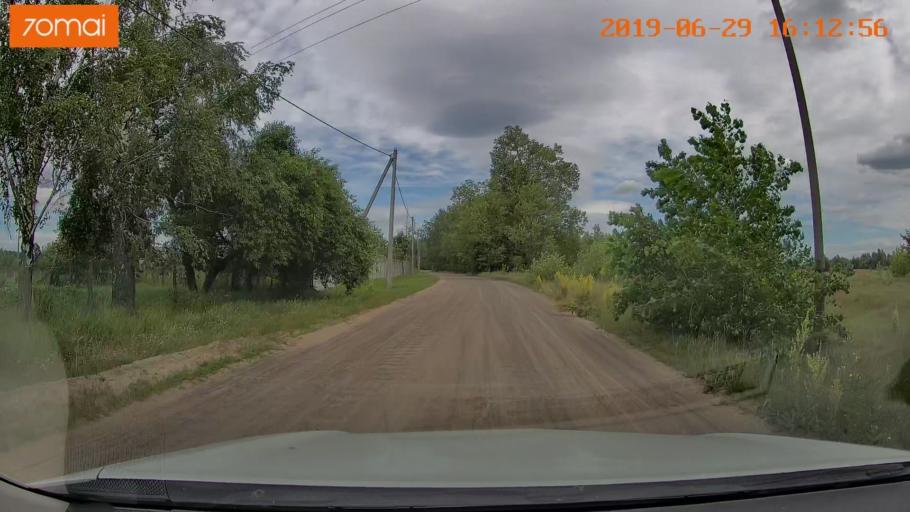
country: BY
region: Brest
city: Luninyets
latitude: 52.1992
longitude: 27.0176
